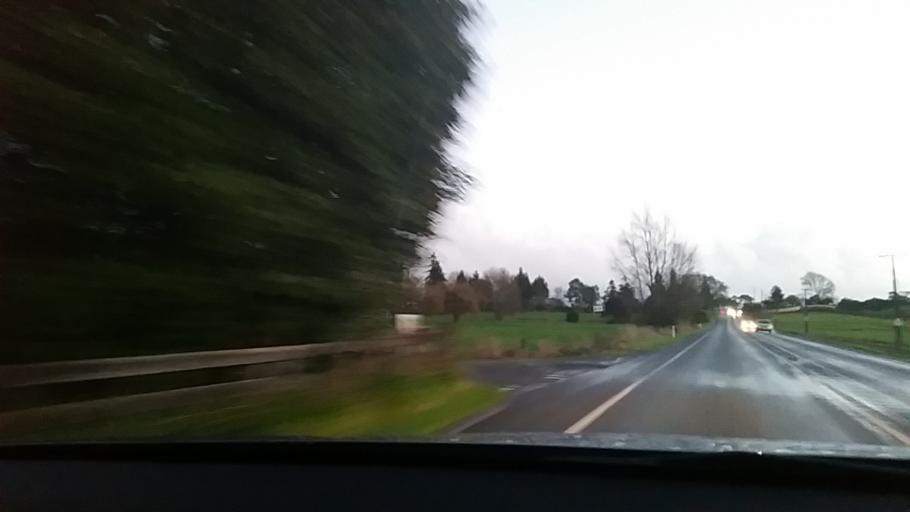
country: NZ
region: Waikato
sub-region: Hamilton City
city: Hamilton
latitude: -37.8120
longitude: 175.2344
